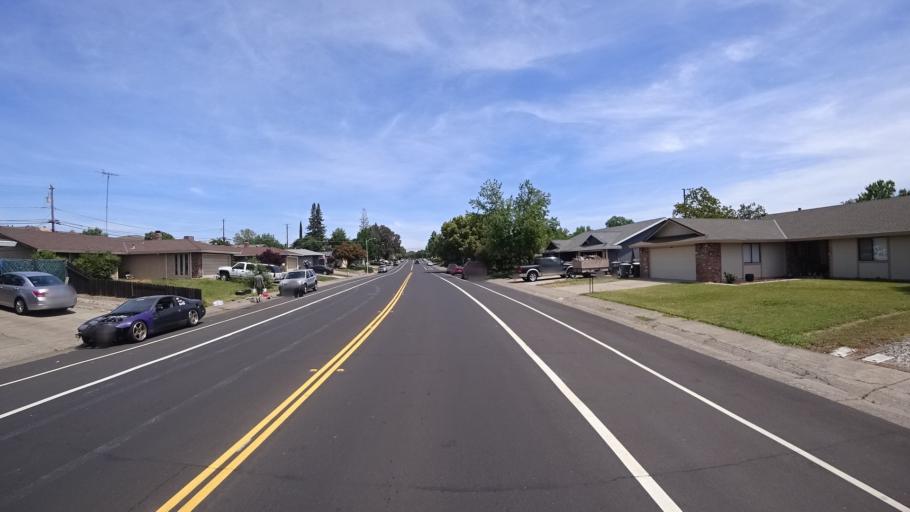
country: US
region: California
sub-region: Placer County
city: Rocklin
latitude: 38.7771
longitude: -121.2435
